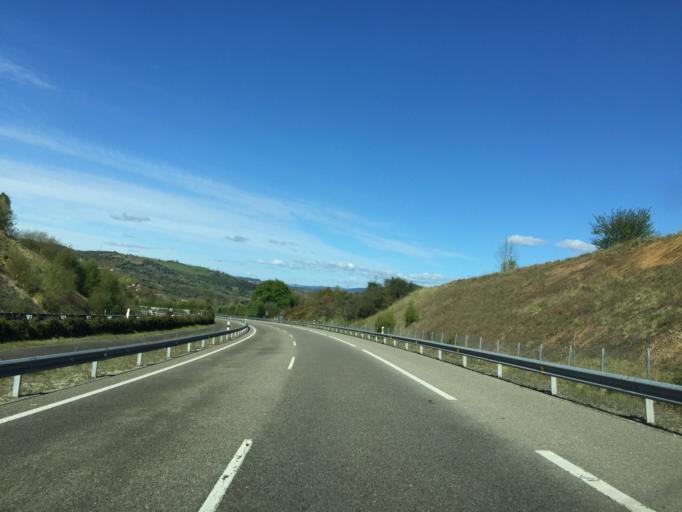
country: ES
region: Asturias
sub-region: Province of Asturias
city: Oviedo
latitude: 43.3531
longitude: -5.9121
